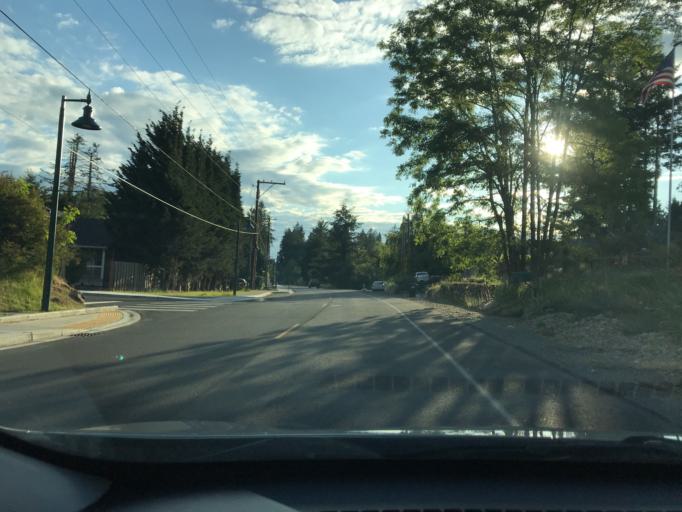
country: US
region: Washington
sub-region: King County
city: Black Diamond
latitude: 47.3122
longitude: -122.0201
